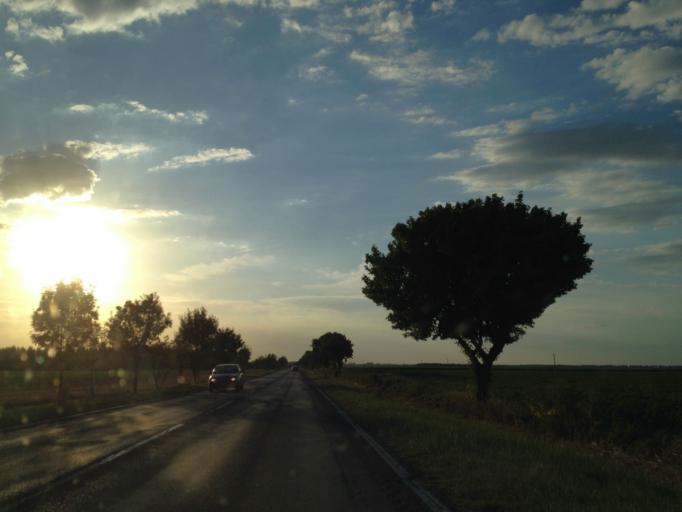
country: HU
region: Gyor-Moson-Sopron
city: Kimle
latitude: 47.7895
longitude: 17.4031
